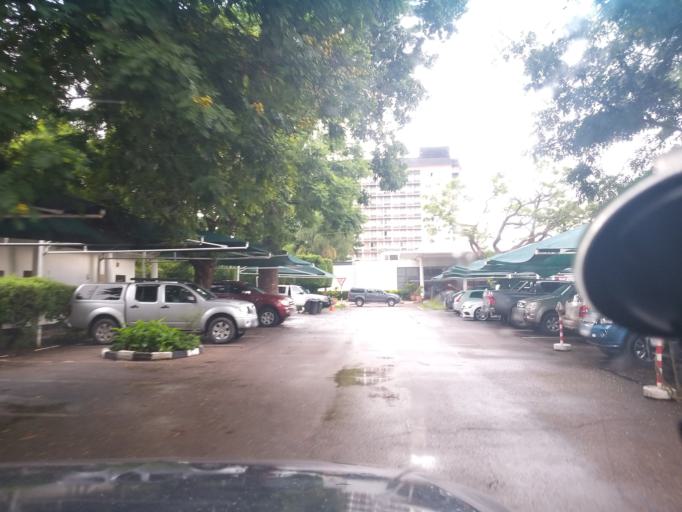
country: ZM
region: Lusaka
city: Lusaka
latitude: -15.4161
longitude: 28.3011
